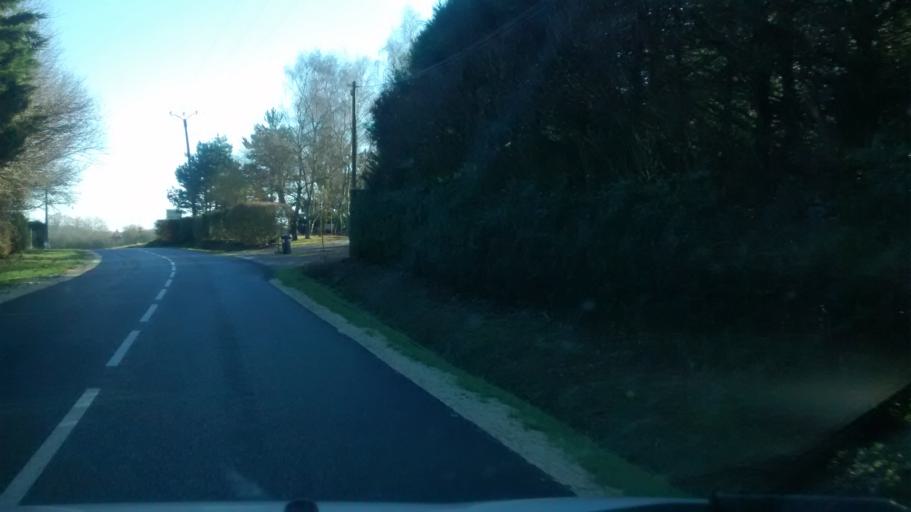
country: FR
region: Centre
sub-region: Departement d'Indre-et-Loire
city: Reugny
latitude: 47.4844
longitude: 0.8531
